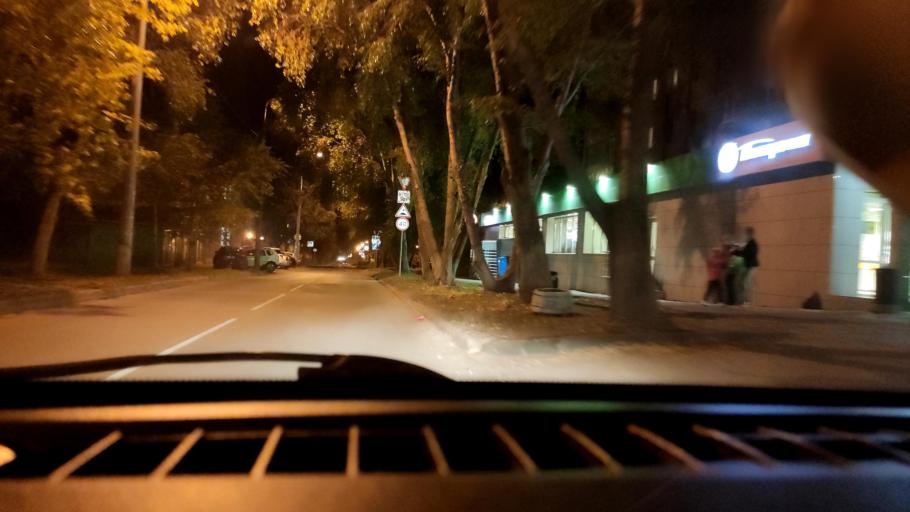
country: RU
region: Samara
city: Samara
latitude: 53.2275
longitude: 50.2486
